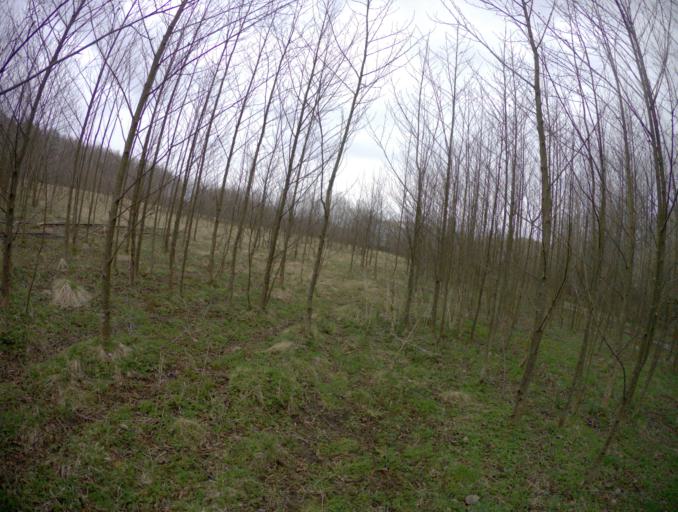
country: RU
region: Vladimir
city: Sudogda
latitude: 56.0148
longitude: 40.8051
